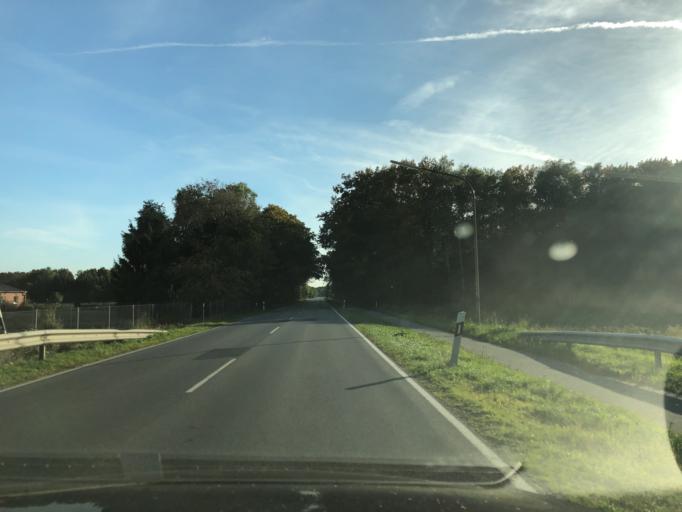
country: DE
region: Lower Saxony
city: Papenburg
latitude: 53.0536
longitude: 7.4056
